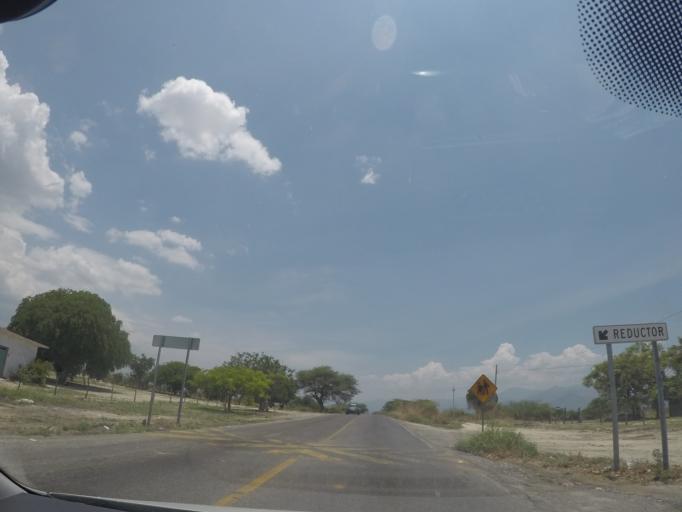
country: MX
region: Oaxaca
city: Santa Maria Jalapa del Marques
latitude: 16.4398
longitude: -95.4661
